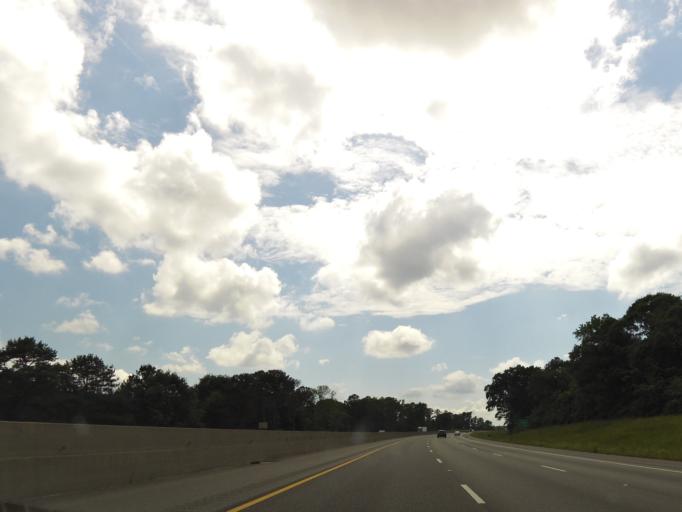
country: US
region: Alabama
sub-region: Calhoun County
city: Oxford
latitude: 33.5862
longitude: -85.8758
